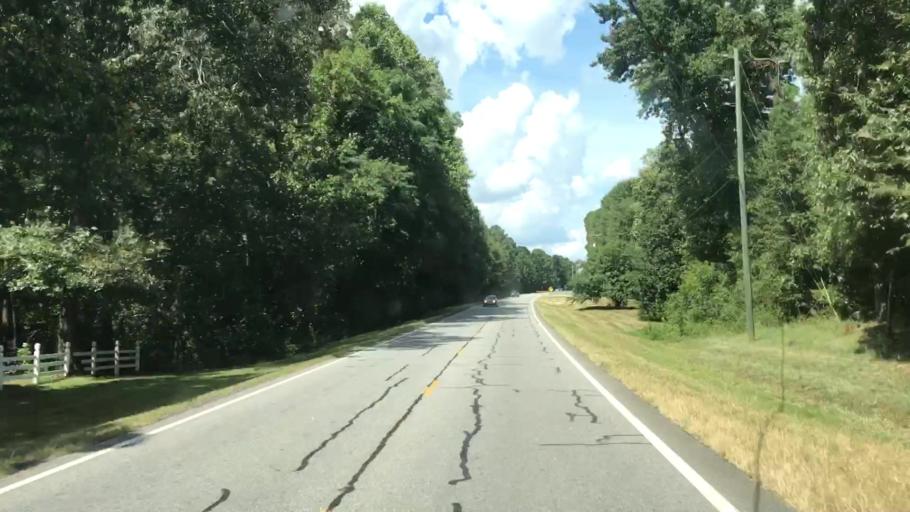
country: US
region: Georgia
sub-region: Oconee County
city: Watkinsville
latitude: 33.8105
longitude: -83.3547
